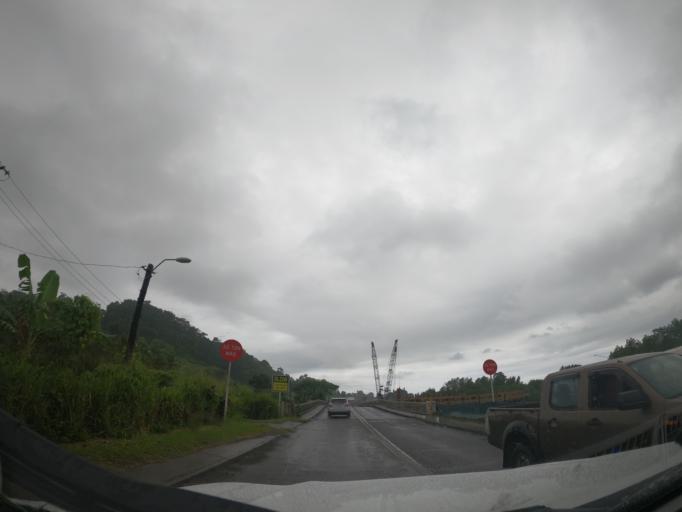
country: FJ
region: Central
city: Suva
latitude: -18.1144
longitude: 178.4310
